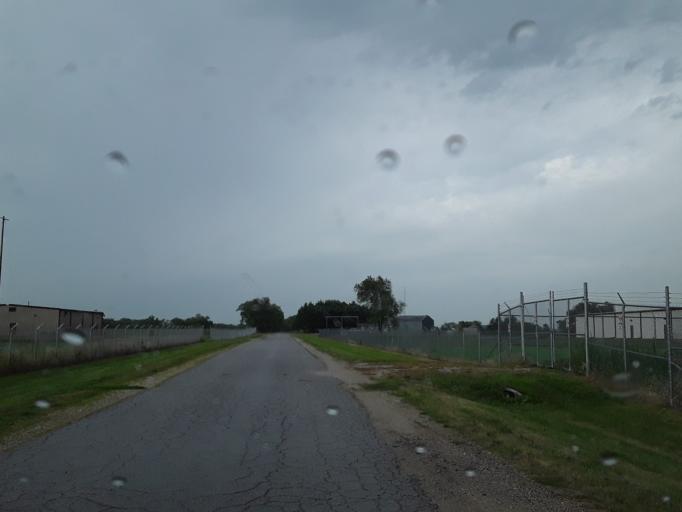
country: US
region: Nebraska
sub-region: Saunders County
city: Yutan
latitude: 41.1856
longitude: -96.4449
